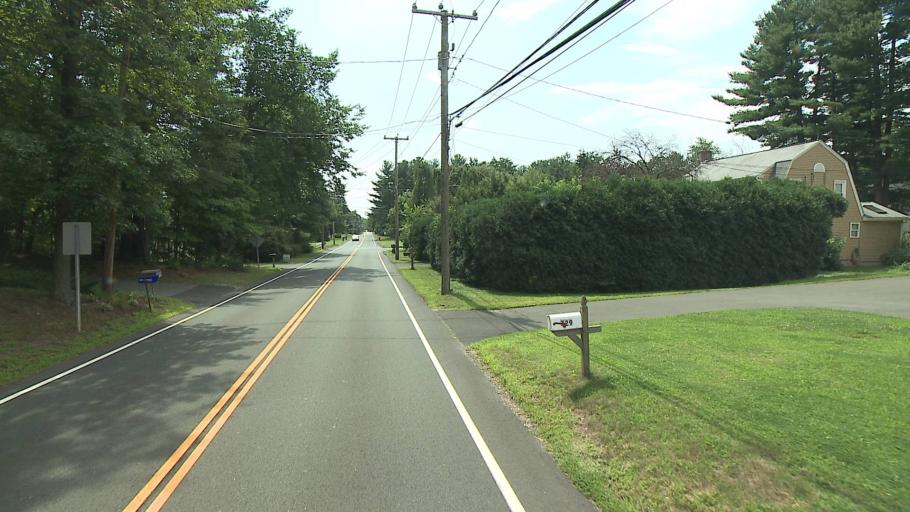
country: US
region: Connecticut
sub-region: Hartford County
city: Collinsville
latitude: 41.7663
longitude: -72.8904
